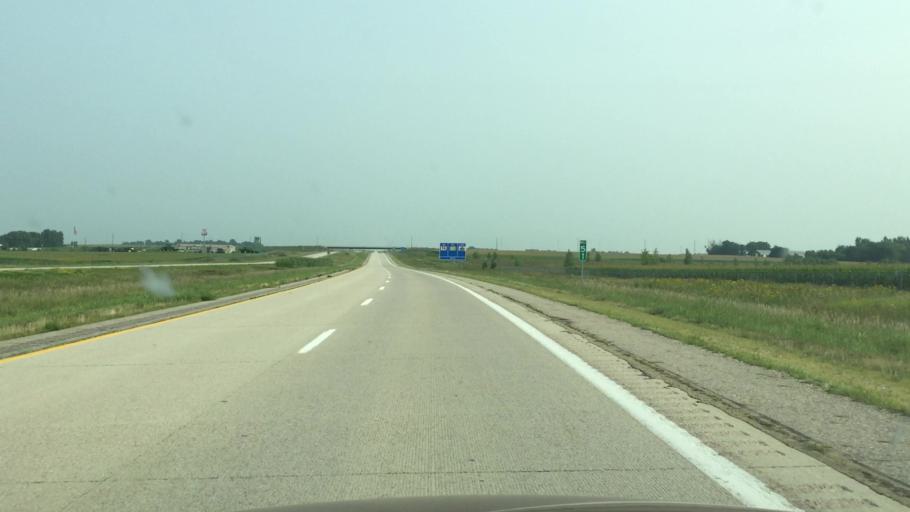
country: US
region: Iowa
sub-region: Osceola County
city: Sibley
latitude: 43.3953
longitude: -95.7171
